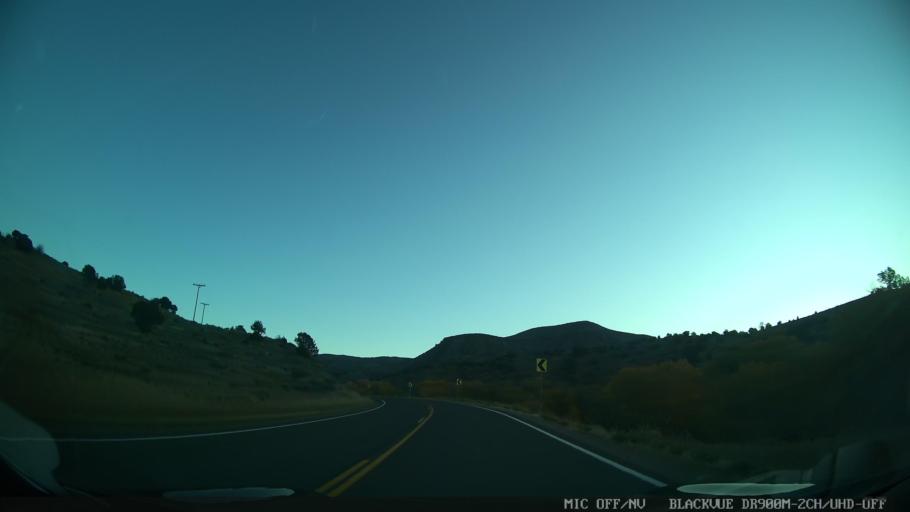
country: US
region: Colorado
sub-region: Eagle County
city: Edwards
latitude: 39.7523
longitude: -106.6717
